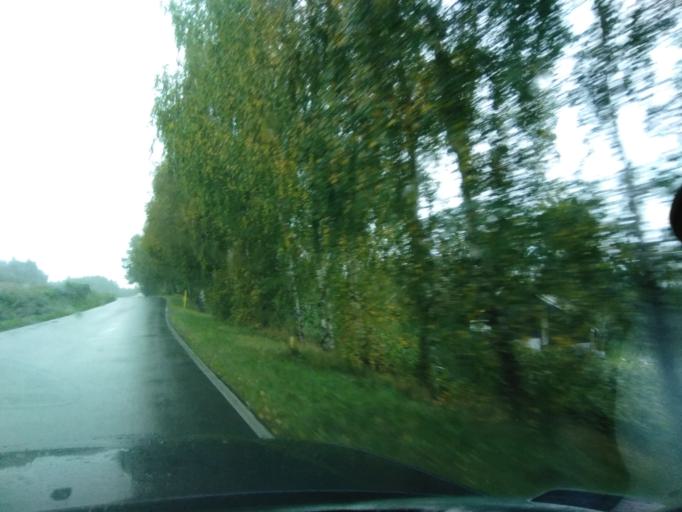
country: PL
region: Subcarpathian Voivodeship
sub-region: Powiat ropczycko-sedziszowski
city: Niedzwiada
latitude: 50.0463
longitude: 21.5391
